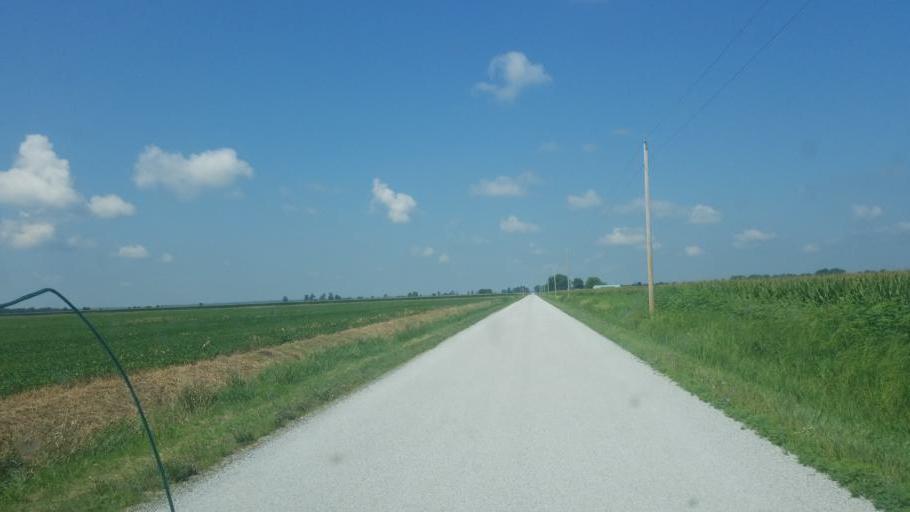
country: US
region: Ohio
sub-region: Hardin County
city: Ada
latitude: 40.6742
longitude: -83.7481
